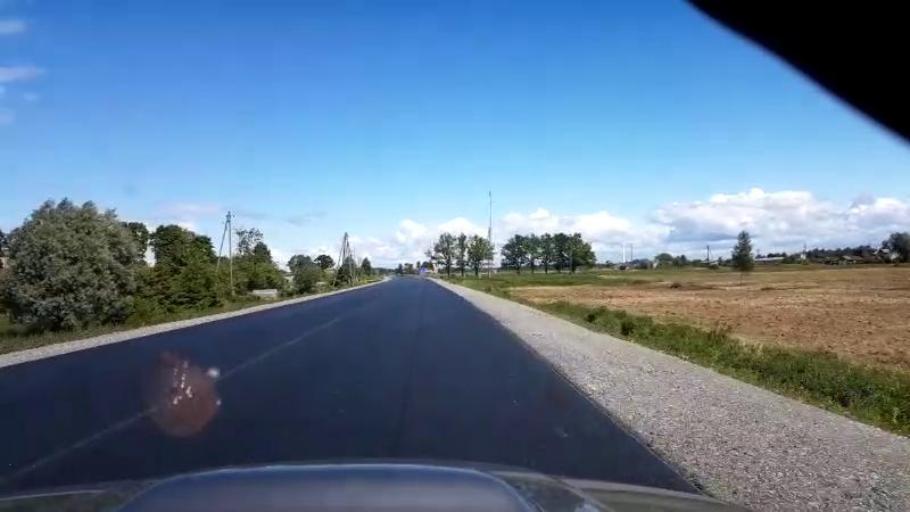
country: LV
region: Salacgrivas
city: Ainazi
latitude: 57.8585
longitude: 24.3667
